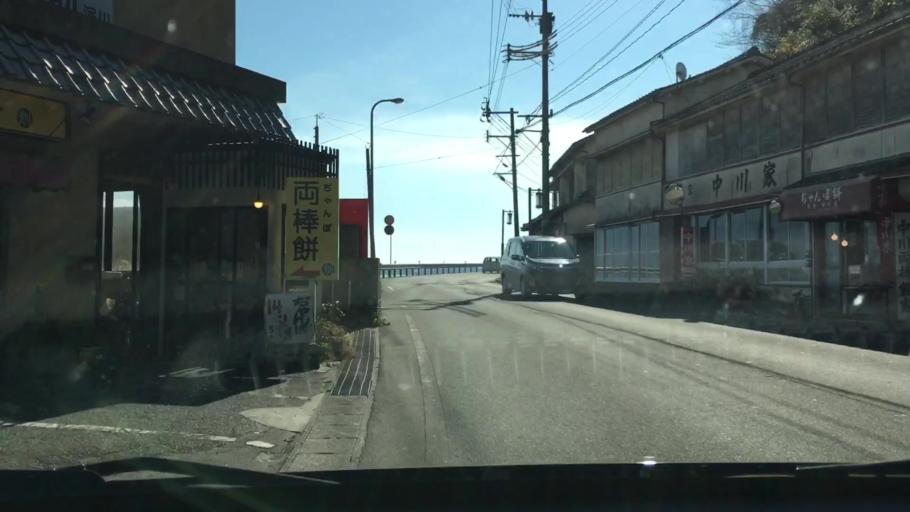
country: JP
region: Kagoshima
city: Kagoshima-shi
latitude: 31.6131
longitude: 130.5748
